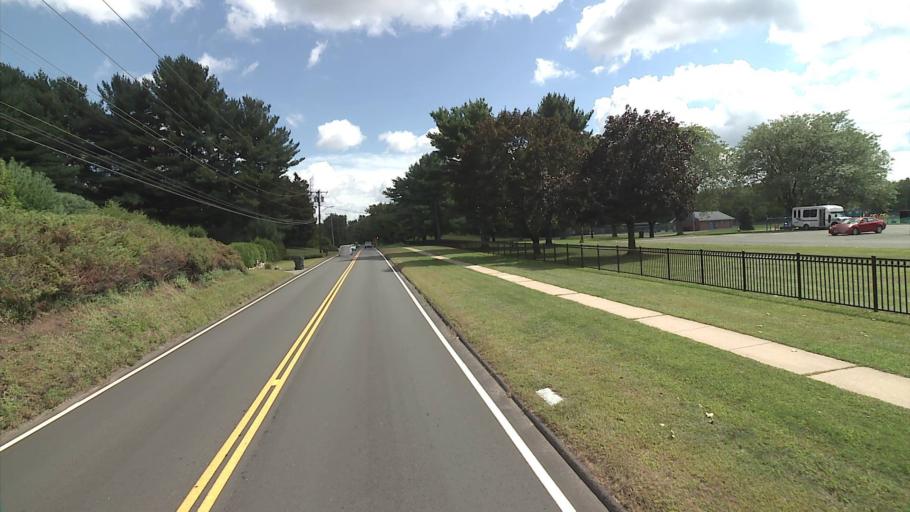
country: US
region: Connecticut
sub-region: Hartford County
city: Wethersfield
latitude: 41.6630
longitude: -72.6518
